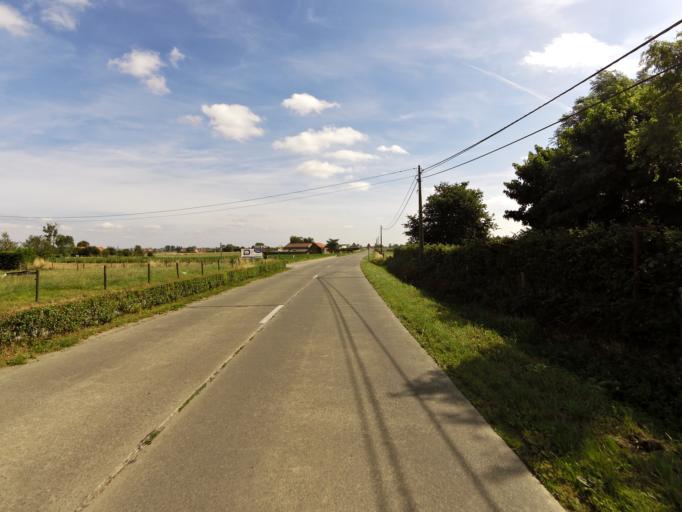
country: BE
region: Flanders
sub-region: Provincie West-Vlaanderen
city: Houthulst
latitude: 50.9614
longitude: 2.8849
